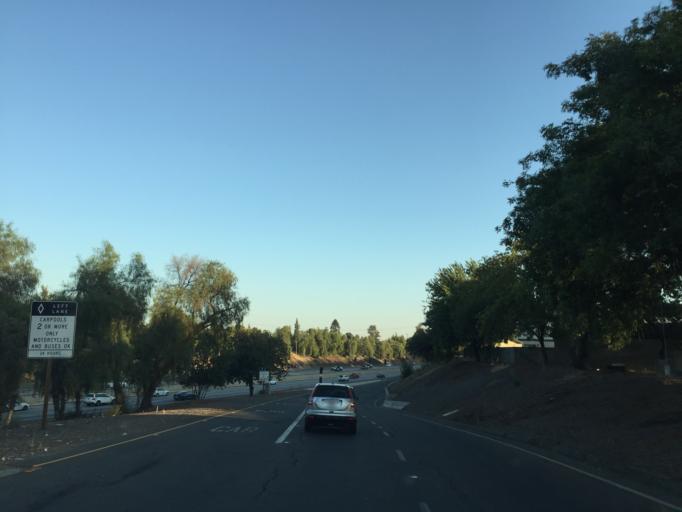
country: US
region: California
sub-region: Fresno County
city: Fresno
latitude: 36.7938
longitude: -119.7858
